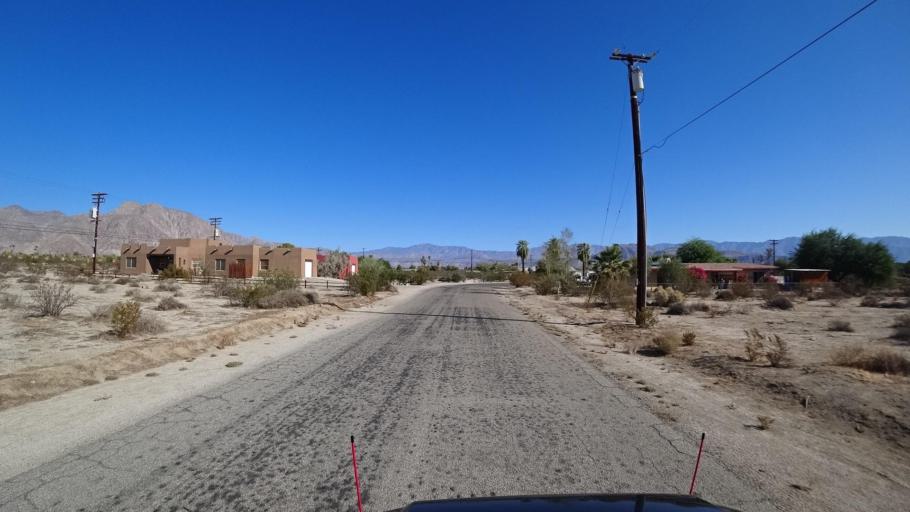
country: US
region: California
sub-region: San Diego County
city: Borrego Springs
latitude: 33.2537
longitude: -116.3732
